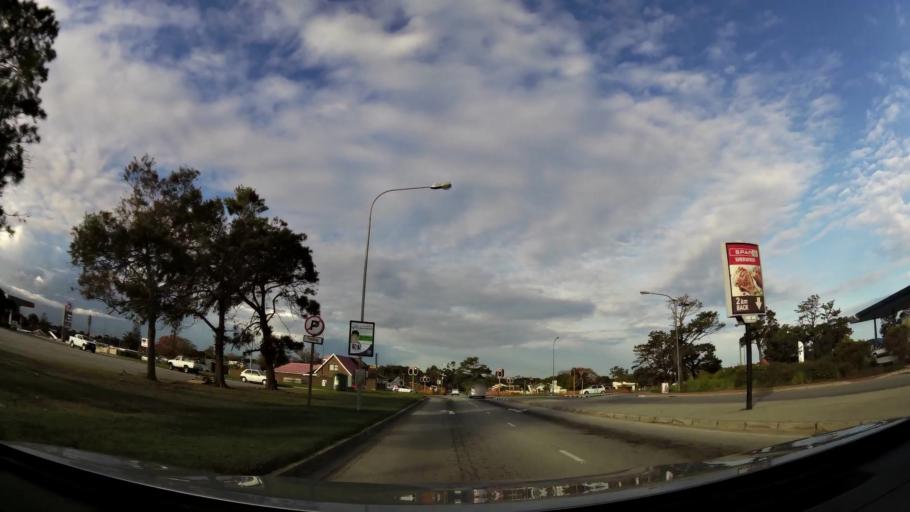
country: ZA
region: Eastern Cape
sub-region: Nelson Mandela Bay Metropolitan Municipality
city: Port Elizabeth
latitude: -33.9569
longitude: 25.5041
